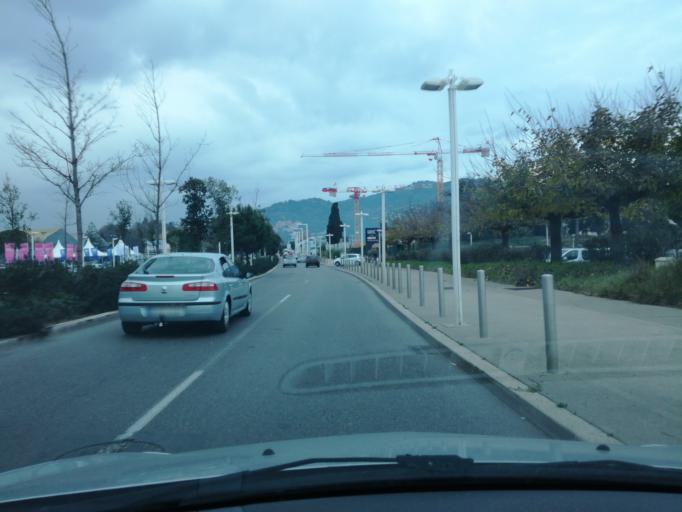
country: FR
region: Provence-Alpes-Cote d'Azur
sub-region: Departement des Alpes-Maritimes
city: Mandelieu-la-Napoule
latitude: 43.5503
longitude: 6.9616
